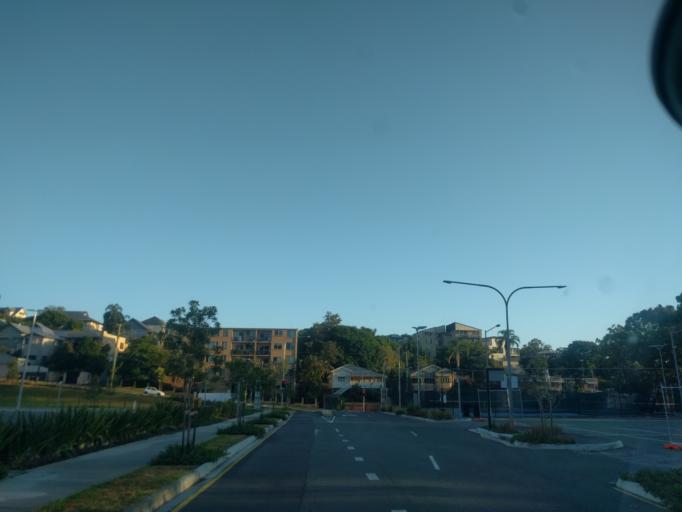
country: AU
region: Queensland
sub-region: Brisbane
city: Spring Hill
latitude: -27.4493
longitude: 153.0180
